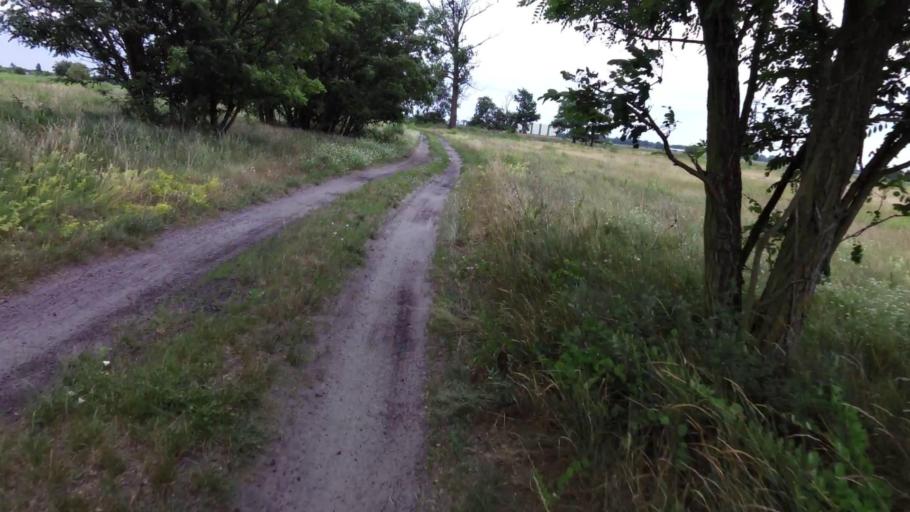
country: PL
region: Lubusz
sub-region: Powiat gorzowski
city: Kostrzyn nad Odra
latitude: 52.6151
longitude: 14.6015
